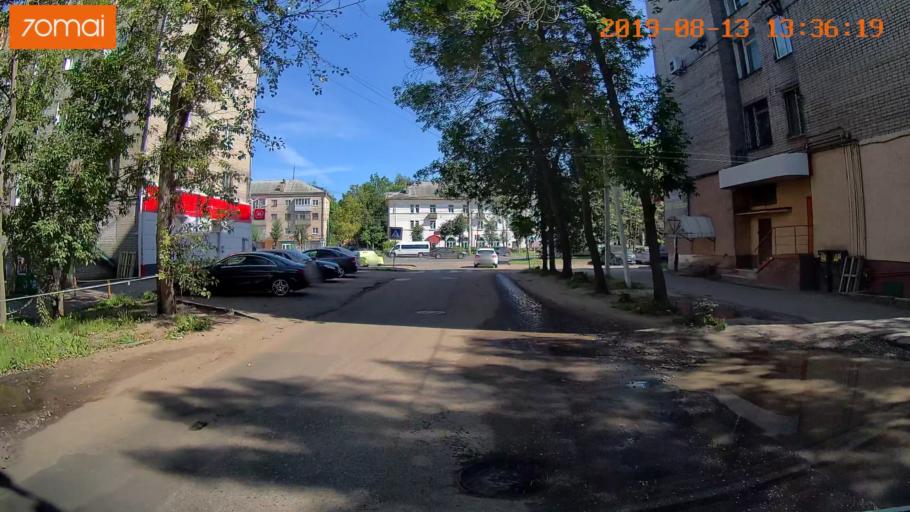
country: RU
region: Ivanovo
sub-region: Gorod Ivanovo
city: Ivanovo
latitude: 56.9690
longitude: 40.9723
